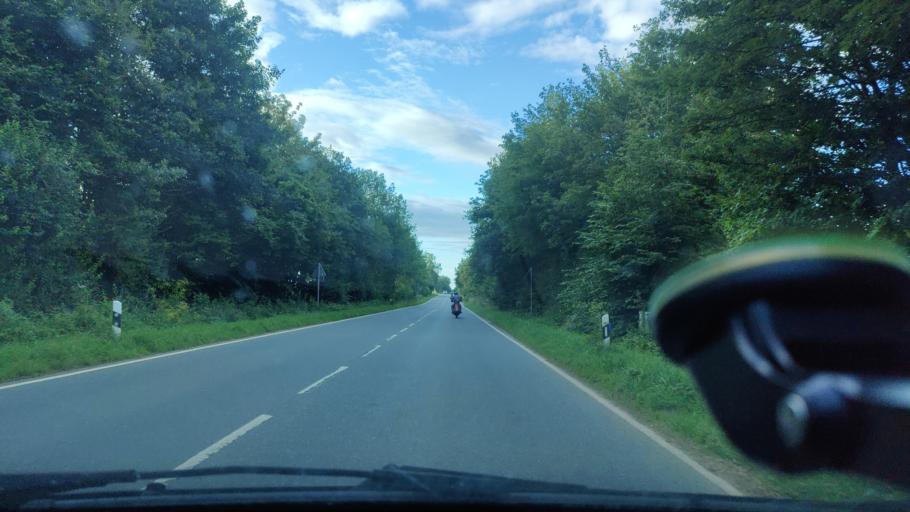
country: DE
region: North Rhine-Westphalia
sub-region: Regierungsbezirk Dusseldorf
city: Schermbeck
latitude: 51.6025
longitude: 6.8898
